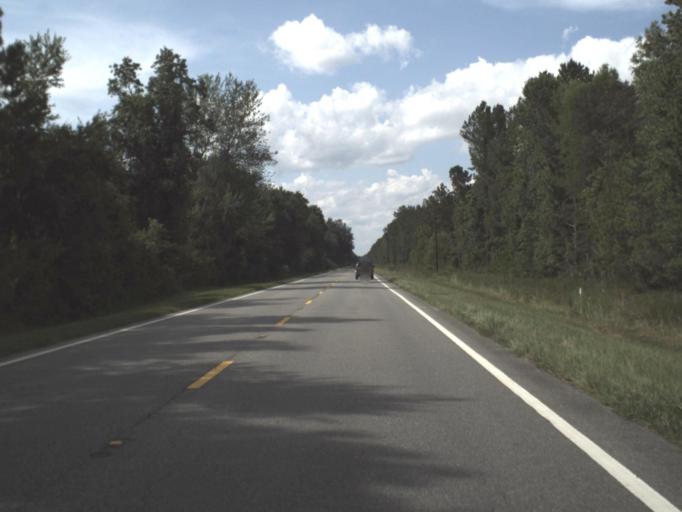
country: US
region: Florida
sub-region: Taylor County
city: Perry
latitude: 30.3153
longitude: -83.6398
